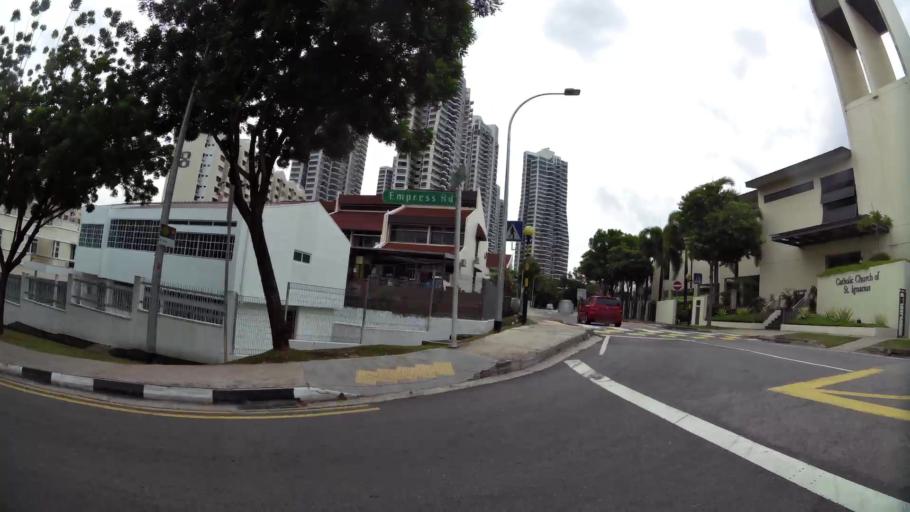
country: SG
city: Singapore
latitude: 1.3177
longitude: 103.8059
